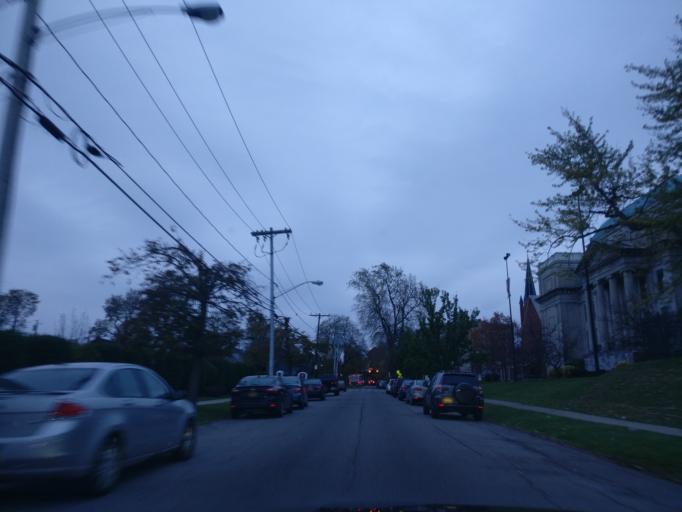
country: US
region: New York
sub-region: Erie County
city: Buffalo
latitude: 42.9045
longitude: -78.8899
